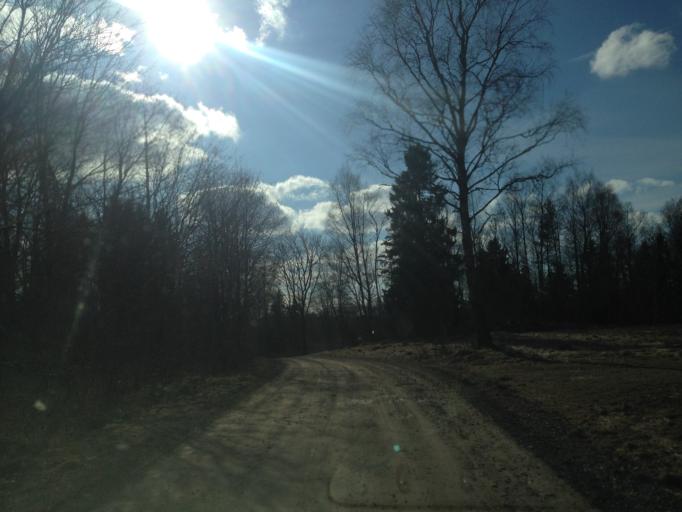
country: EE
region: Harju
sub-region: Nissi vald
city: Riisipere
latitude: 59.1383
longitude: 24.4366
